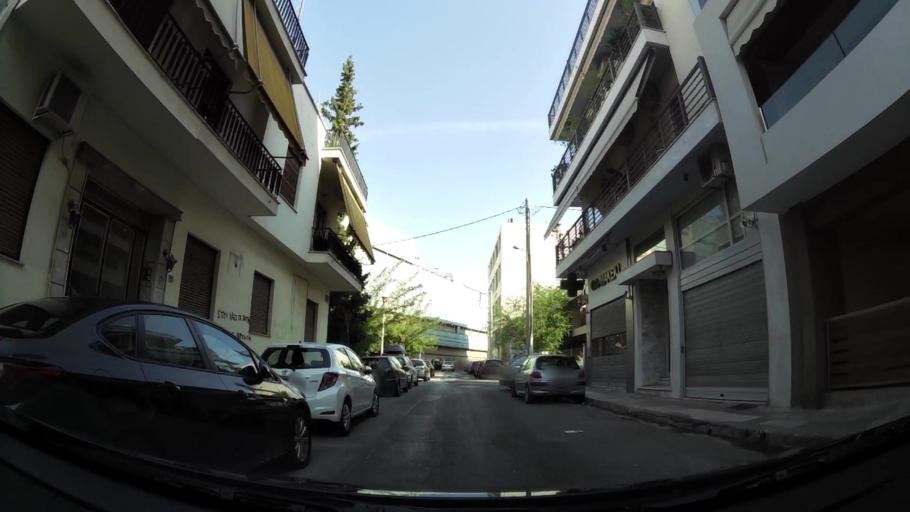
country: GR
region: Attica
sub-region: Nomarchia Athinas
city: Athens
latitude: 37.9735
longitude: 23.7096
